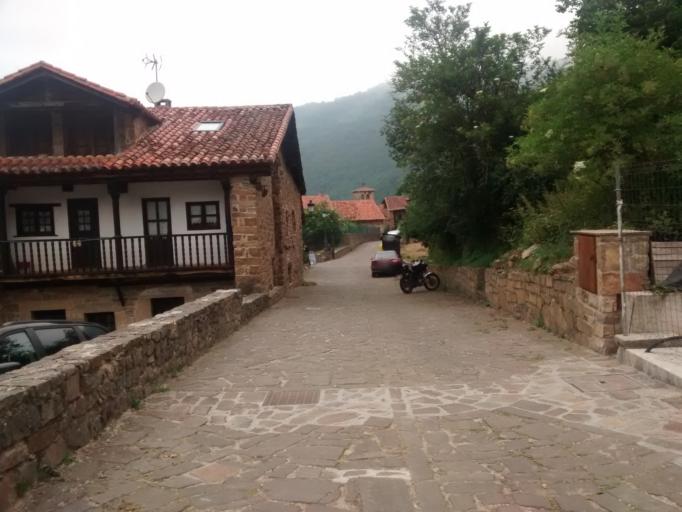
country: ES
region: Cantabria
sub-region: Provincia de Cantabria
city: Pesquera
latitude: 43.1424
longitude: -4.1920
